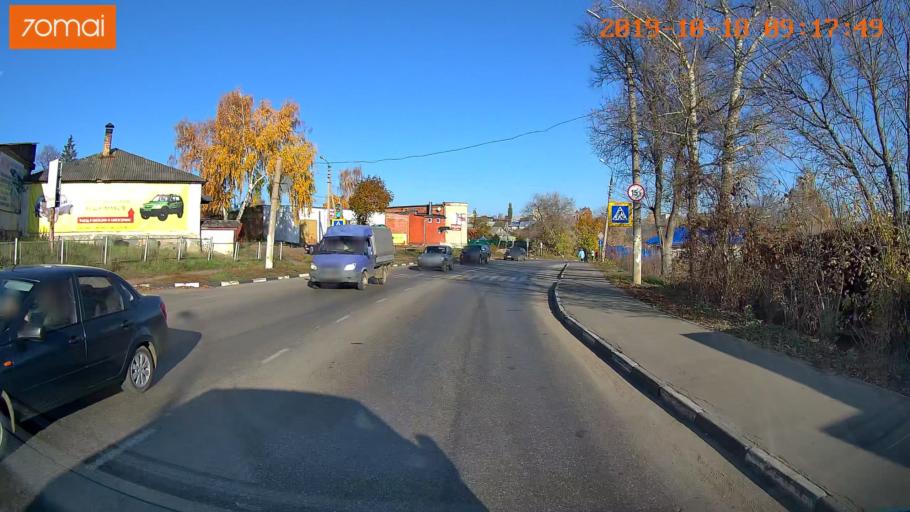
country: RU
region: Tula
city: Yefremov
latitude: 53.1354
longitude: 38.1160
